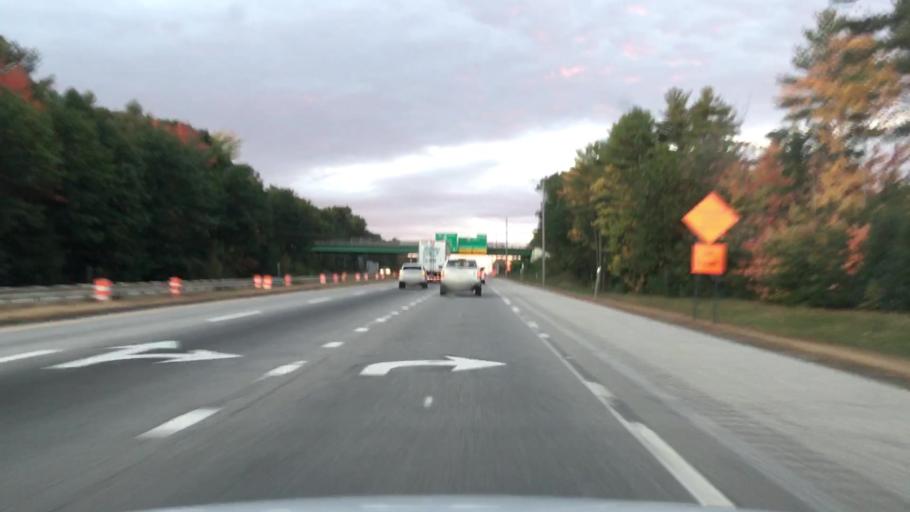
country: US
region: Maine
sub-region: Cumberland County
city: South Portland Gardens
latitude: 43.6205
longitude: -70.3562
